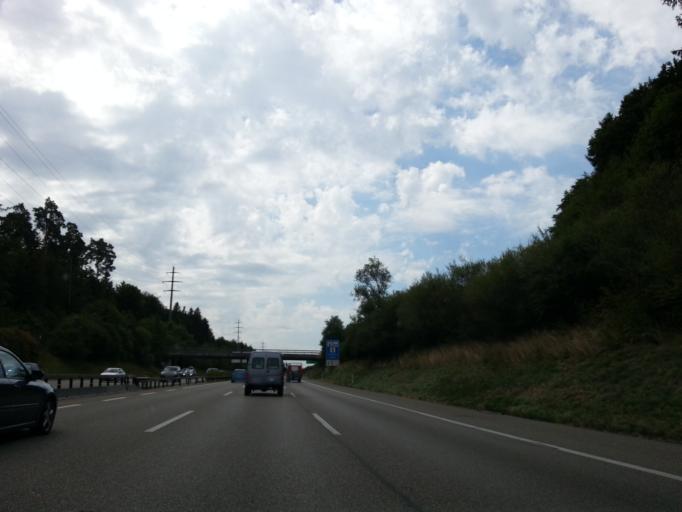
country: CH
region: Bern
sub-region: Bern-Mittelland District
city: Urtenen
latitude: 47.0064
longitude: 7.4949
